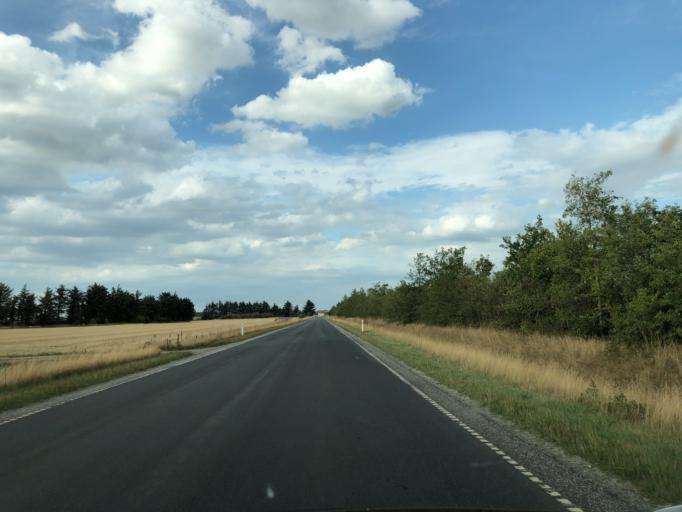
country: DK
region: Central Jutland
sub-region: Holstebro Kommune
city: Holstebro
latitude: 56.3885
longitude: 8.4544
